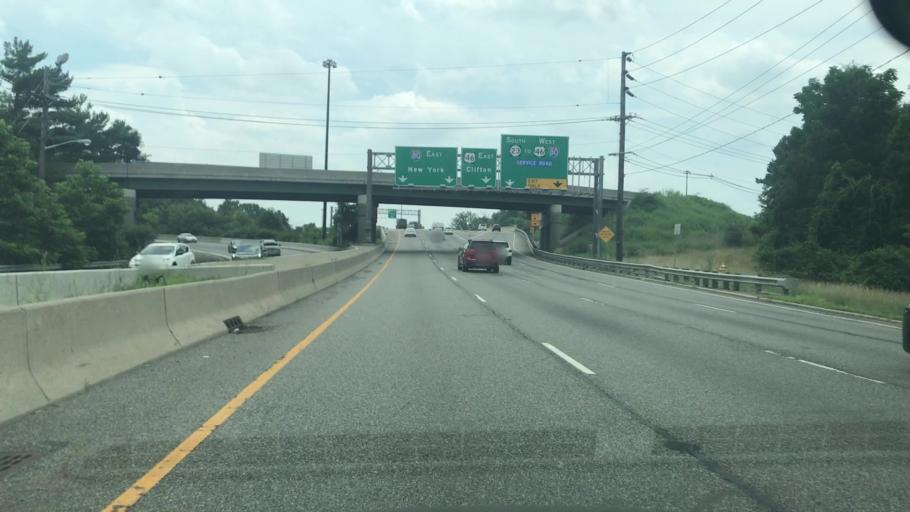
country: US
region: New Jersey
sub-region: Passaic County
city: Singac
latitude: 40.8985
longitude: -74.2540
